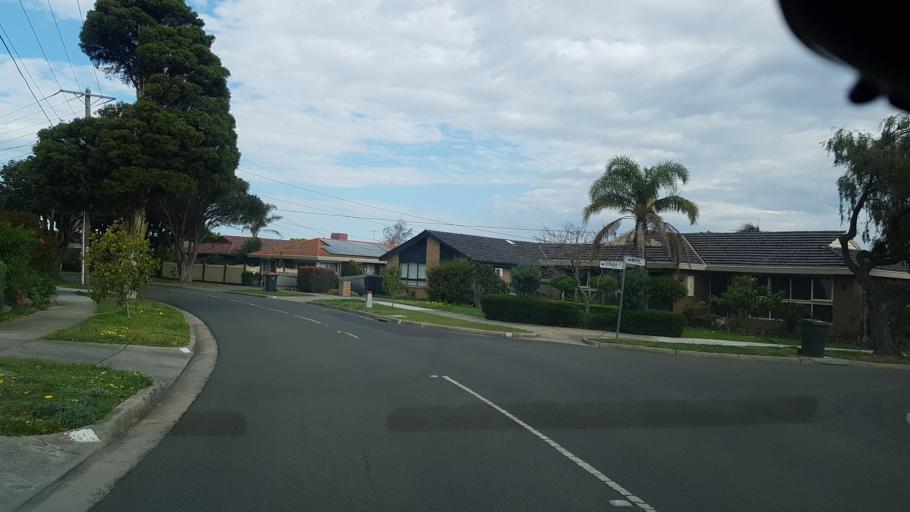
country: AU
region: Victoria
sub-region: Monash
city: Notting Hill
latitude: -37.9109
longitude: 145.1671
